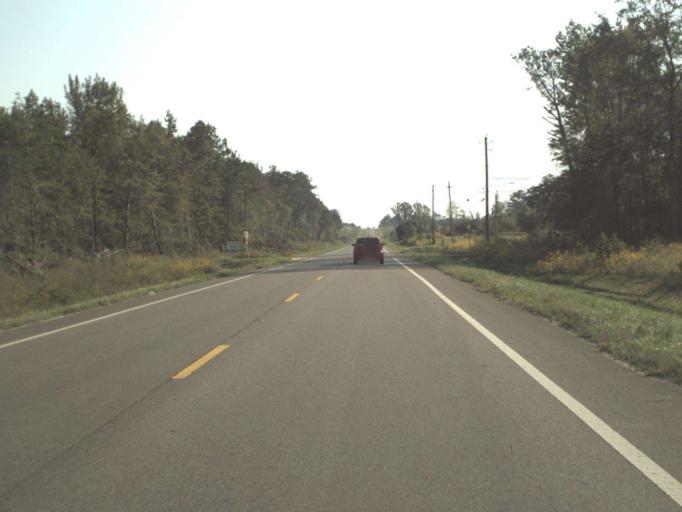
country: US
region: Florida
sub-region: Holmes County
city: Bonifay
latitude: 30.5888
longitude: -85.7940
